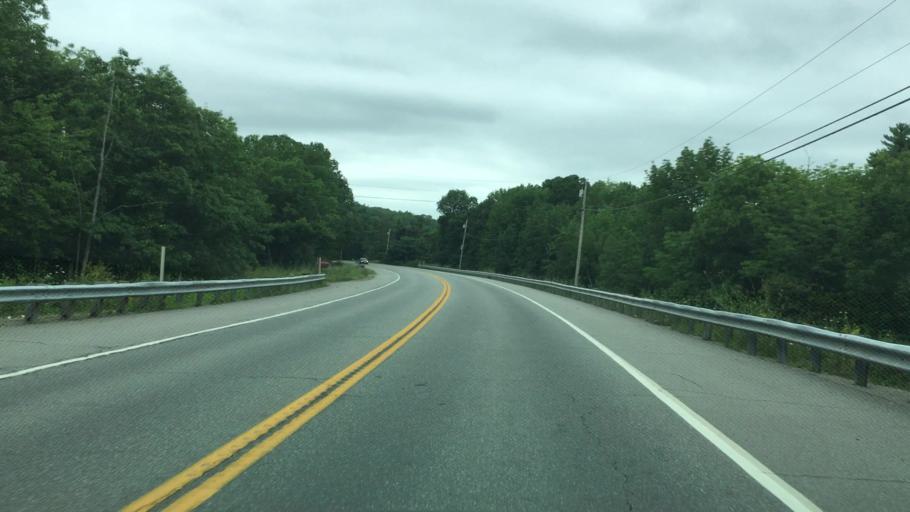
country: US
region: Maine
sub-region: Waldo County
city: Winterport
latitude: 44.6647
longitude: -68.8313
